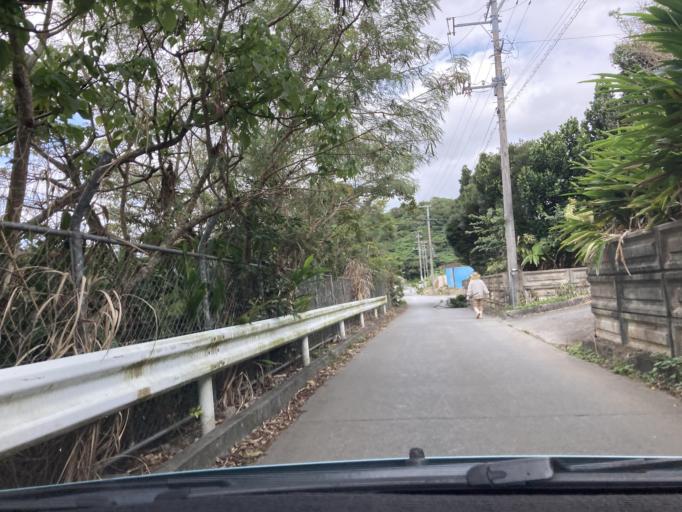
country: JP
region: Okinawa
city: Ginowan
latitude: 26.2144
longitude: 127.7417
